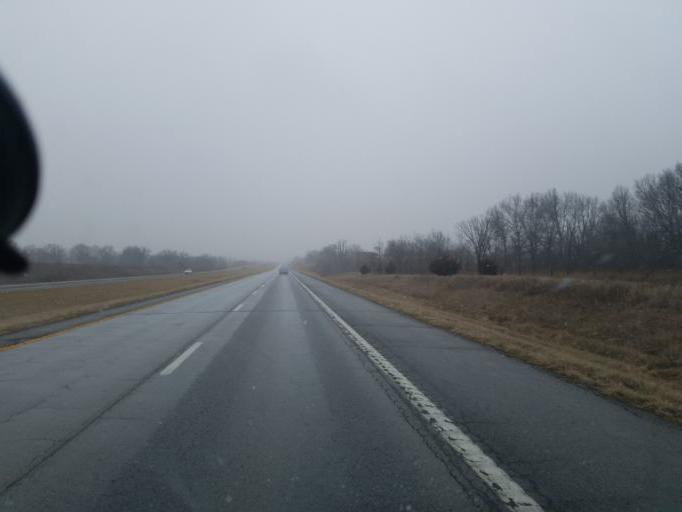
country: US
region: Missouri
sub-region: Macon County
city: La Plata
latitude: 39.9747
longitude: -92.4763
